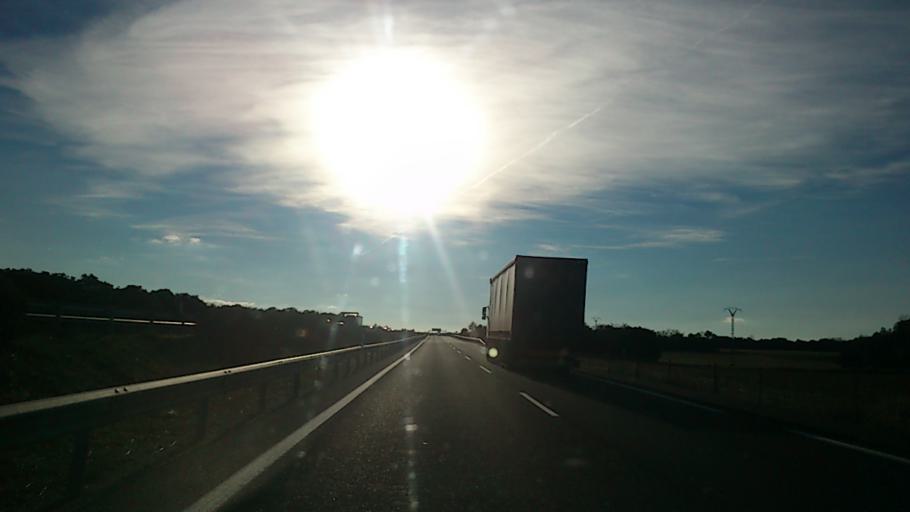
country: ES
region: Castille-La Mancha
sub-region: Provincia de Guadalajara
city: Mirabueno
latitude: 40.9229
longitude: -2.7240
